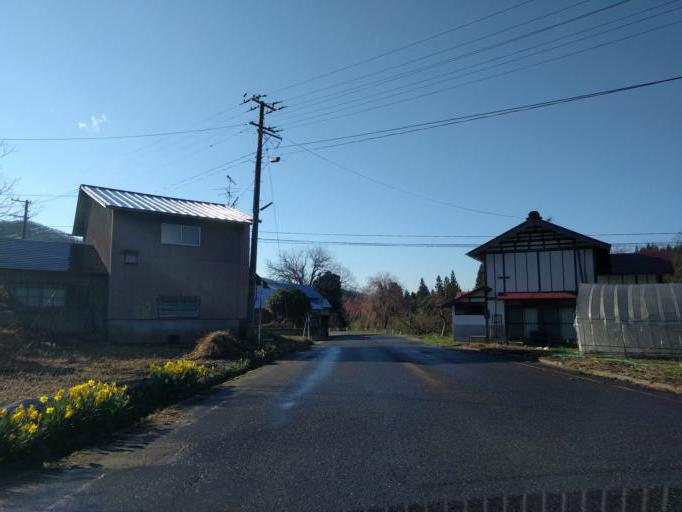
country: JP
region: Fukushima
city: Kitakata
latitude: 37.7069
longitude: 139.7831
